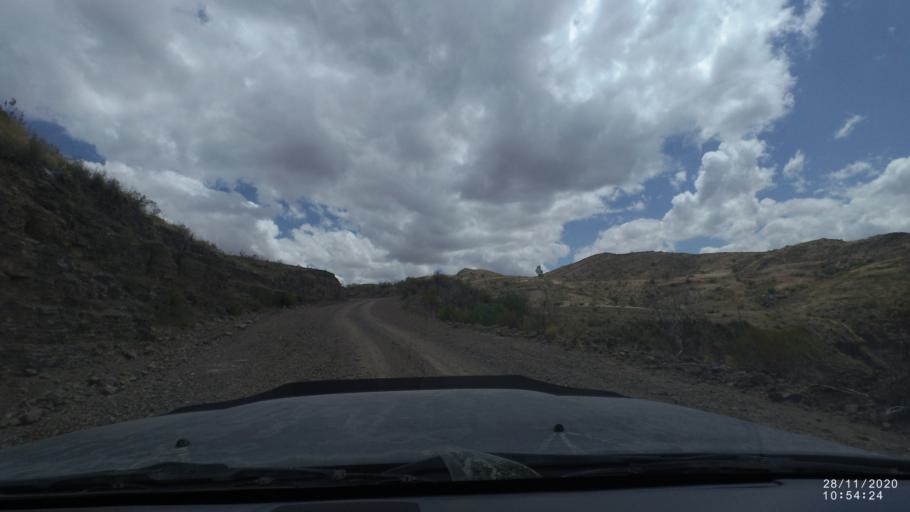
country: BO
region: Cochabamba
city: Capinota
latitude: -17.7782
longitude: -66.1200
